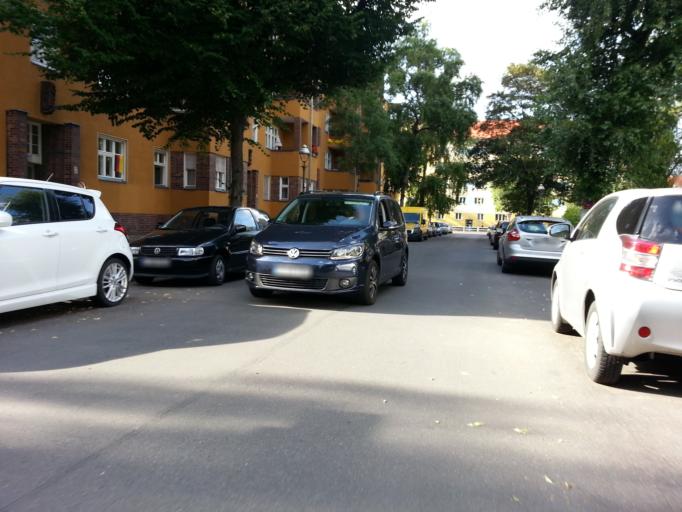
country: DE
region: Berlin
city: Charlottenburg-Nord
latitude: 52.5284
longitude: 13.3012
